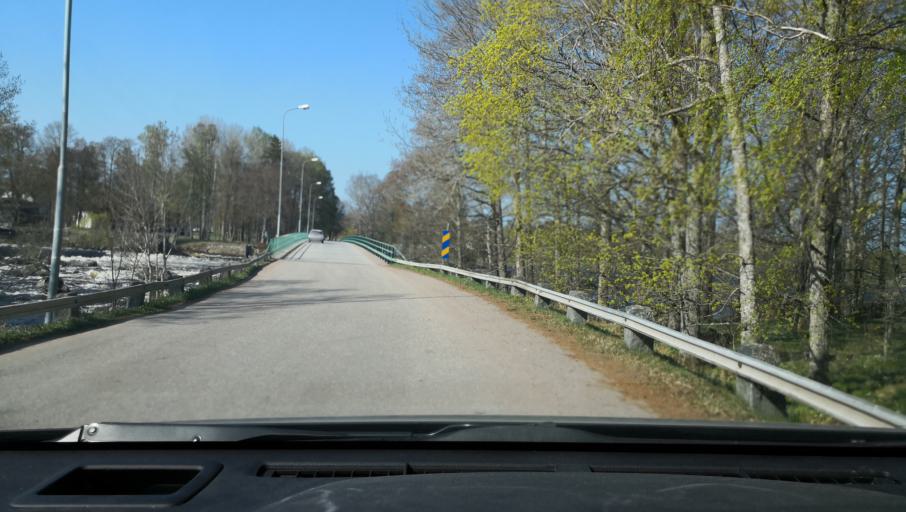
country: SE
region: Uppsala
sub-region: Heby Kommun
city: Tarnsjo
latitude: 60.2852
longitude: 16.8842
